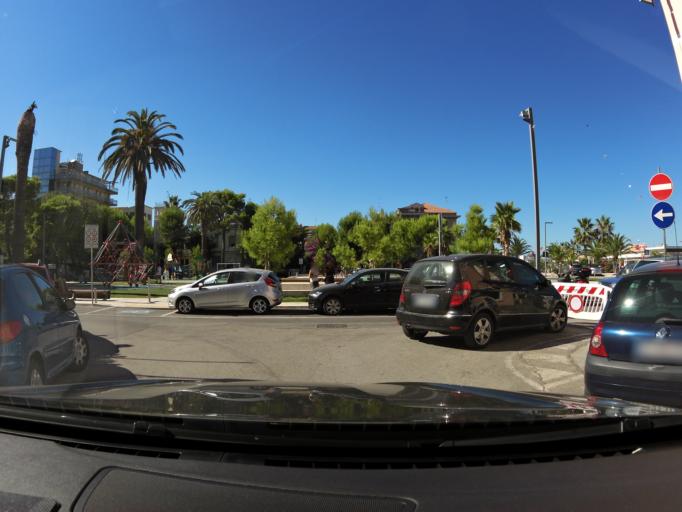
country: IT
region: The Marches
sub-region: Province of Fermo
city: Porto San Giorgio
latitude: 43.1819
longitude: 13.7978
